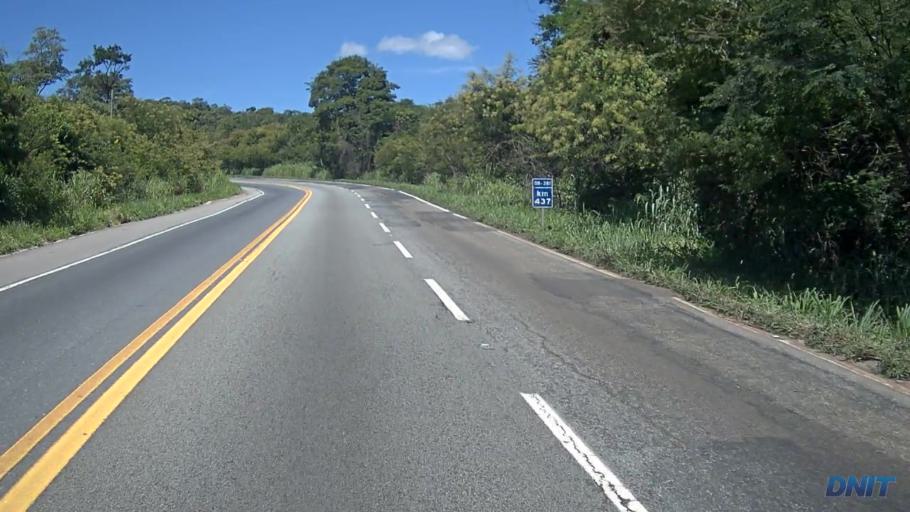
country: BR
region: Minas Gerais
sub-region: Caete
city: Caete
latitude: -19.7874
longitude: -43.7347
